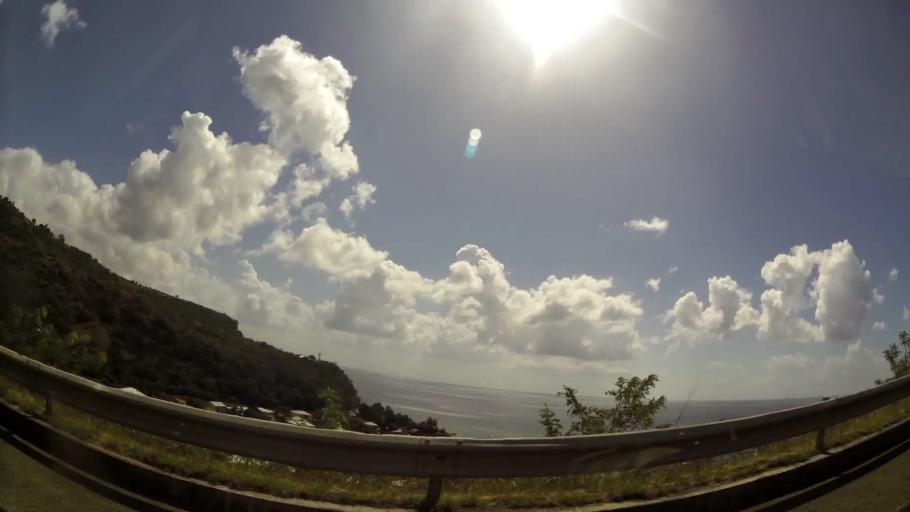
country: MQ
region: Martinique
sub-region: Martinique
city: Saint-Pierre
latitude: 14.6795
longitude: -61.1679
